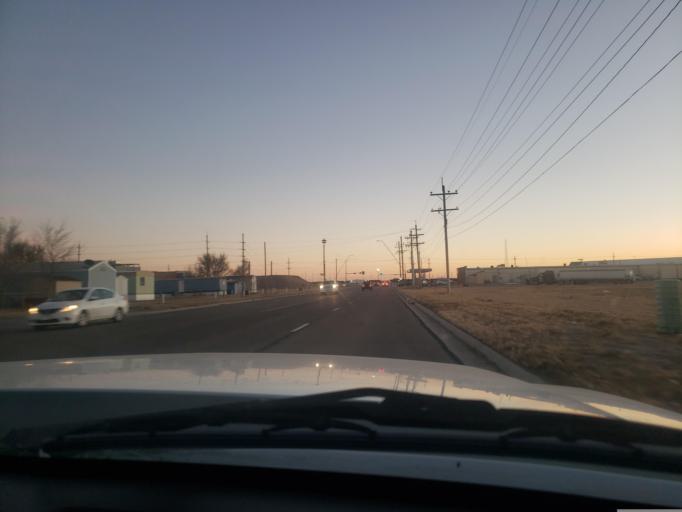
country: US
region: Kansas
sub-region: Finney County
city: Garden City
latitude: 37.9626
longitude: -100.8291
